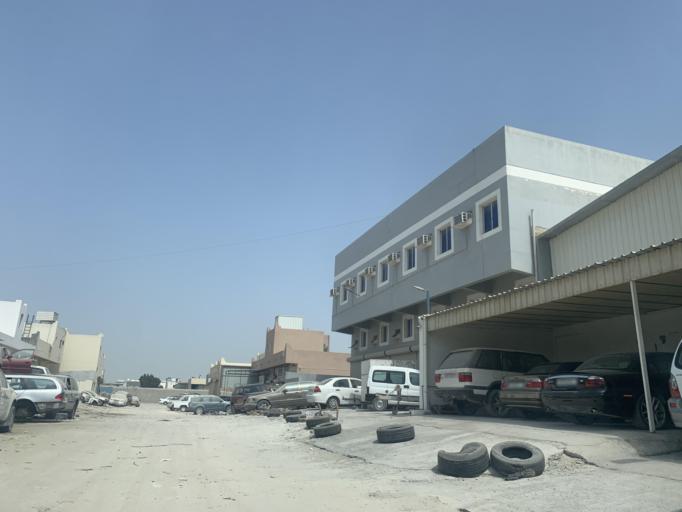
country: BH
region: Central Governorate
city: Madinat Hamad
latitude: 26.1424
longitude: 50.4826
